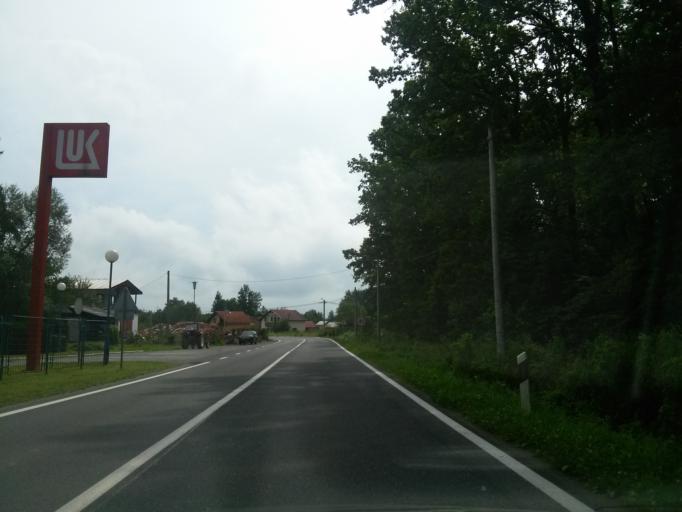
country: HR
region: Sisacko-Moslavacka
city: Glina
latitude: 45.3414
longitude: 16.0426
